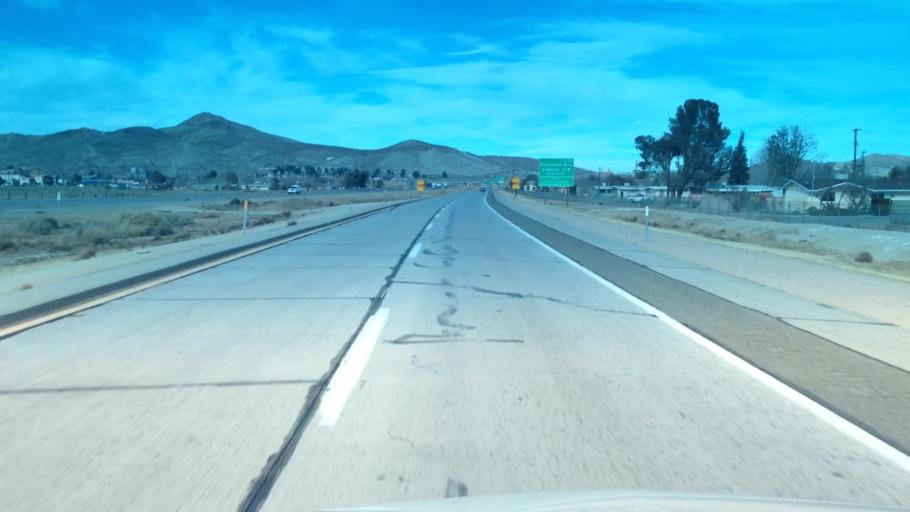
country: US
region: California
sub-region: Kern County
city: Rosamond
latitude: 34.8563
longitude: -118.1714
